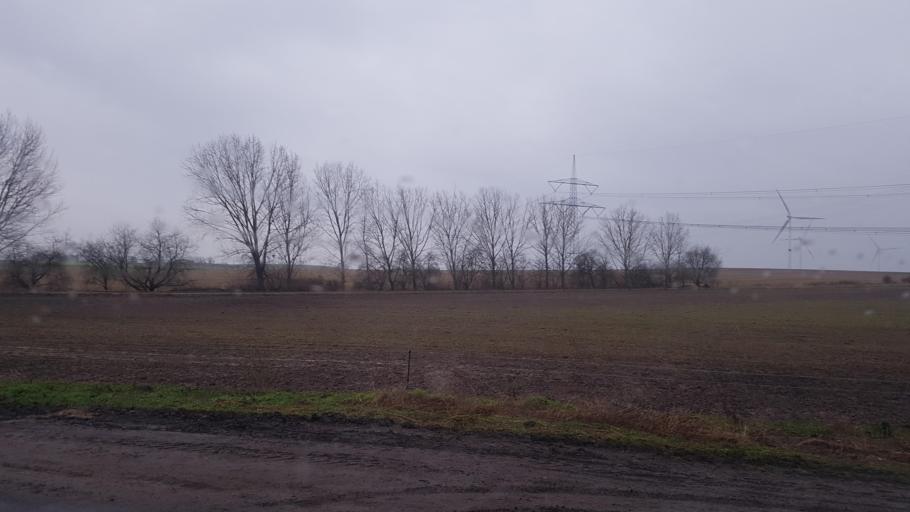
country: DE
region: Brandenburg
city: Zehdenick
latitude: 52.9703
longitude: 13.2736
